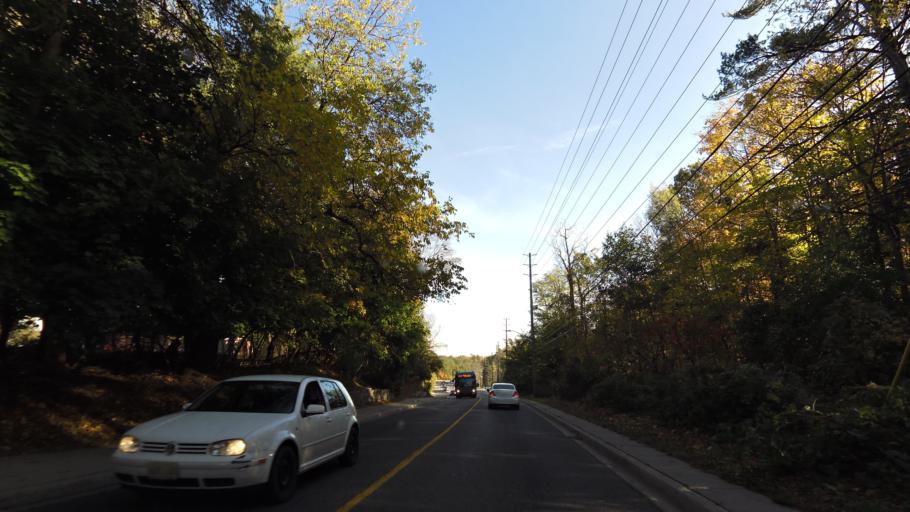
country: CA
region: Ontario
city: Mississauga
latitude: 43.5461
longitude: -79.6650
